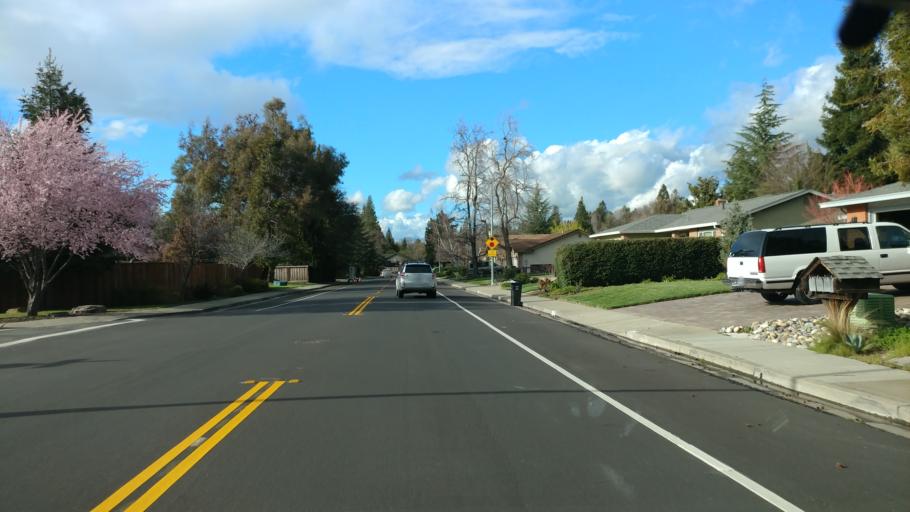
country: US
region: California
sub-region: Contra Costa County
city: San Ramon
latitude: 37.7988
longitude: -121.9740
